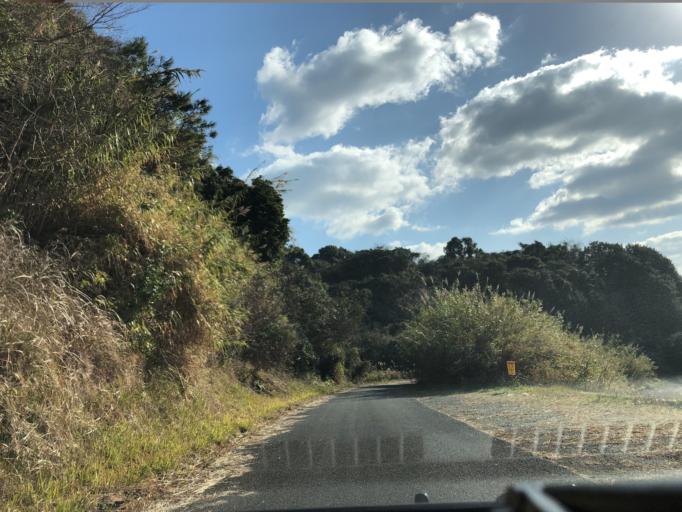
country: JP
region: Kochi
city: Sukumo
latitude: 32.9125
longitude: 132.6939
